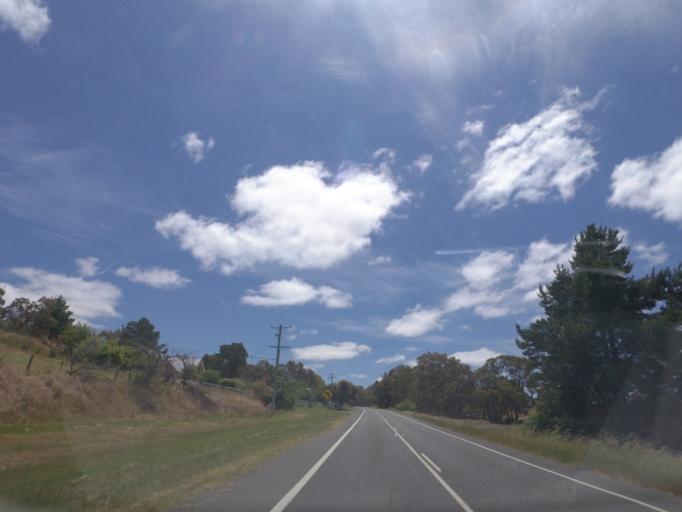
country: AU
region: Victoria
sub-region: Mount Alexander
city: Castlemaine
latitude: -37.2867
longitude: 144.1619
